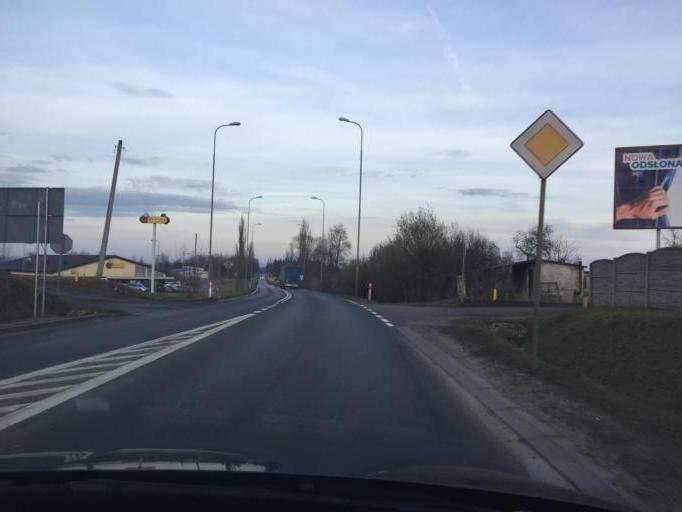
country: PL
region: Lubusz
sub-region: Powiat zielonogorski
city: Nowogrod Bobrzanski
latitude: 51.7980
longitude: 15.2508
